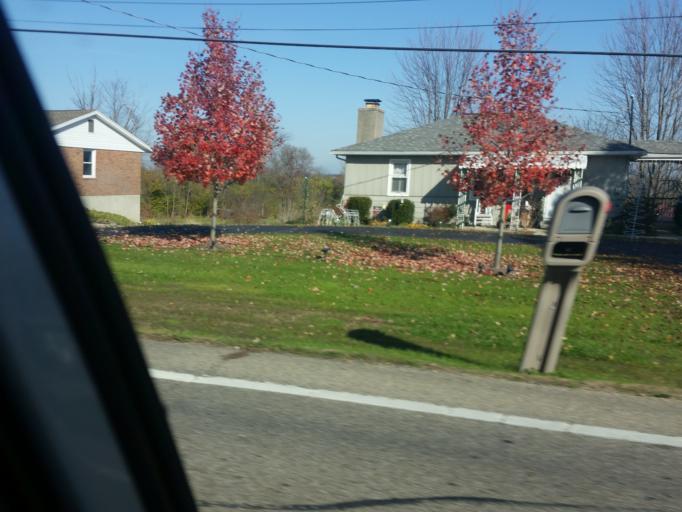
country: US
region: Ohio
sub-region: Butler County
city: Oxford
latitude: 39.4794
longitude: -84.7122
